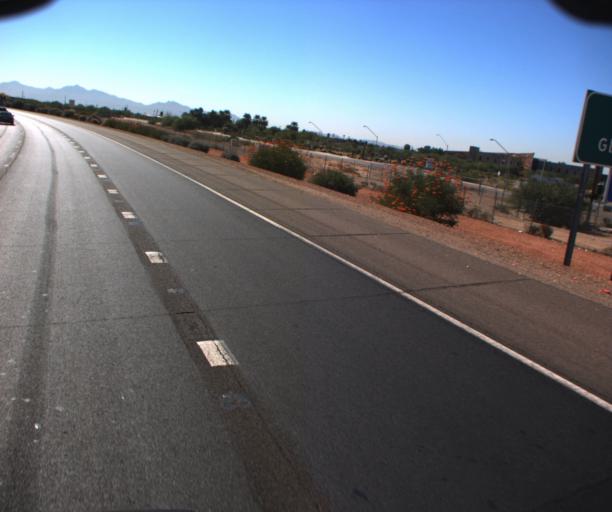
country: US
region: Arizona
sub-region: Maricopa County
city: Peoria
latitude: 33.5446
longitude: -112.2718
